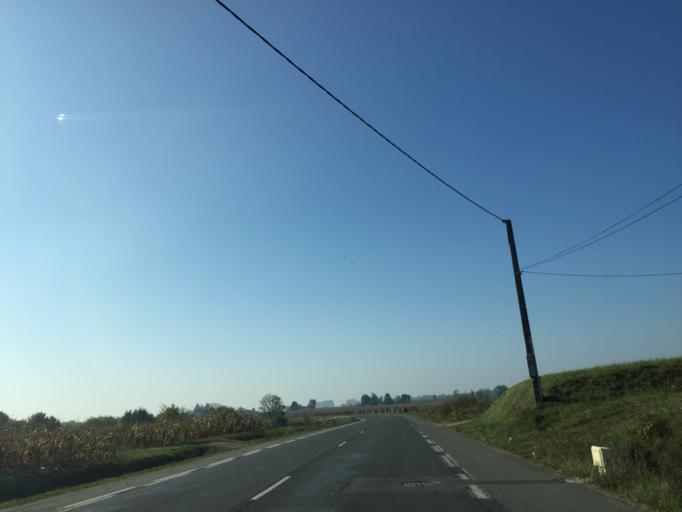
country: FR
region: Rhone-Alpes
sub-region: Departement de l'Ain
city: Miribel
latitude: 45.8289
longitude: 4.9383
